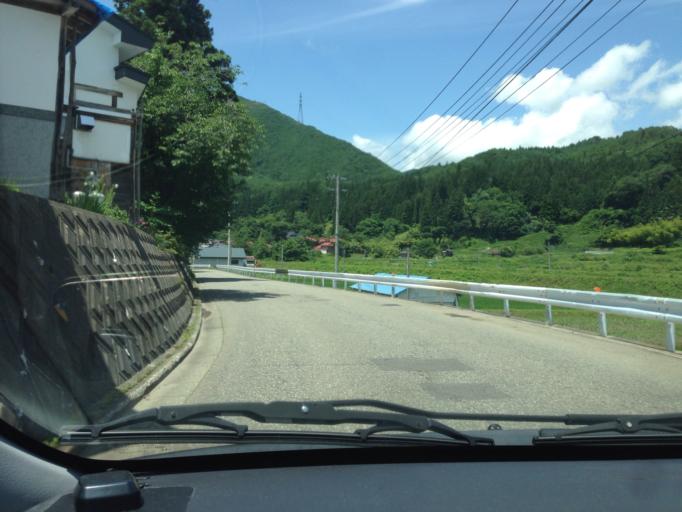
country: JP
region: Tochigi
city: Kuroiso
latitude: 37.2658
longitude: 139.8501
